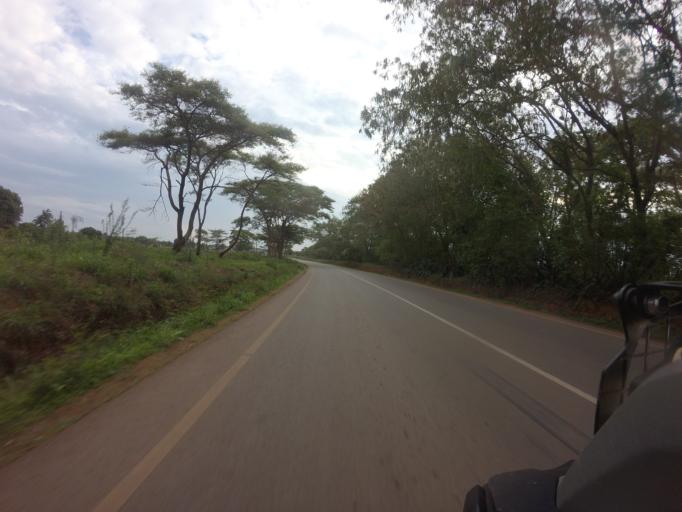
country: ZM
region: Lusaka
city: Lusaka
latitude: -15.5085
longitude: 28.2281
